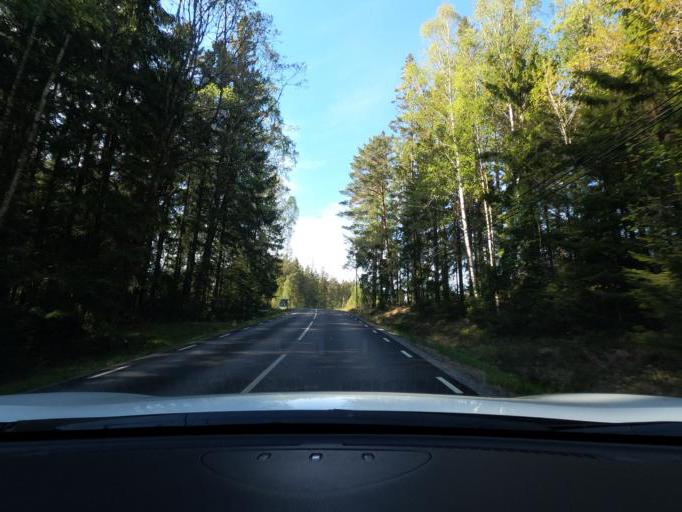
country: SE
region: Vaestra Goetaland
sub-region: Harryda Kommun
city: Landvetter
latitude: 57.6202
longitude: 12.2785
